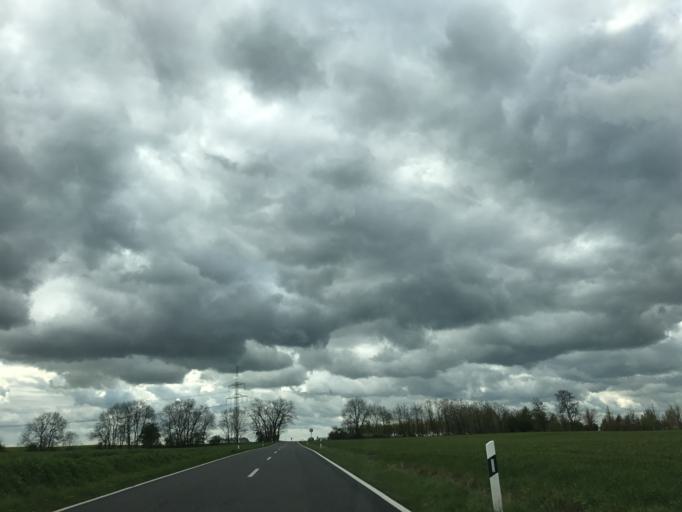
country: DE
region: Brandenburg
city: Pawesin
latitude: 52.5665
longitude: 12.7684
